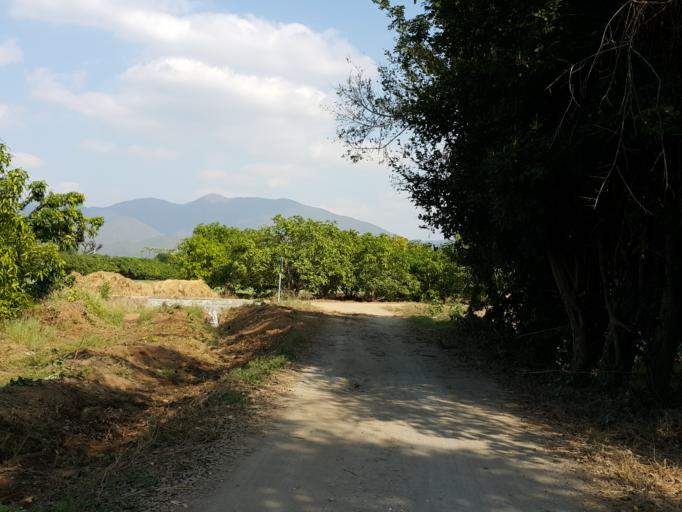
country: TH
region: Lamphun
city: Ban Hong
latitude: 18.2805
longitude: 98.8207
